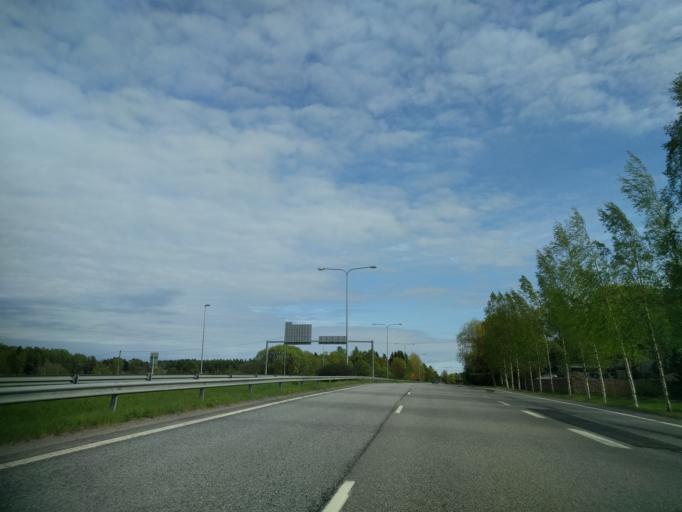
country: FI
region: Varsinais-Suomi
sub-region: Turku
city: Raisio
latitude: 60.4861
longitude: 22.1771
